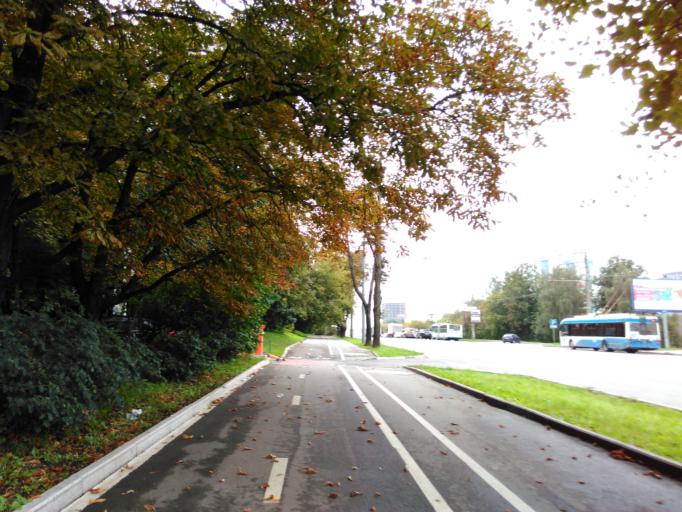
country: RU
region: Moscow
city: Vorob'yovo
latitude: 55.7177
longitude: 37.5197
